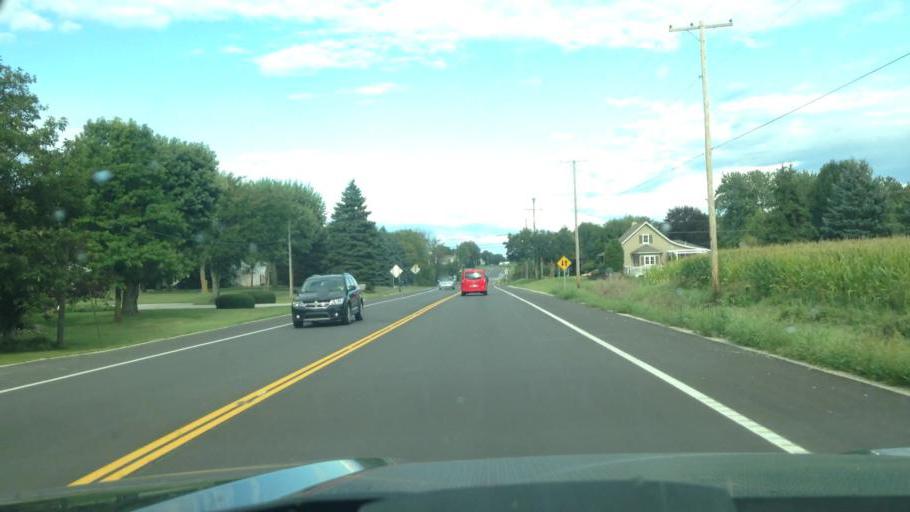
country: US
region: Ohio
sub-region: Darke County
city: Greenville
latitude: 40.1001
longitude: -84.6008
